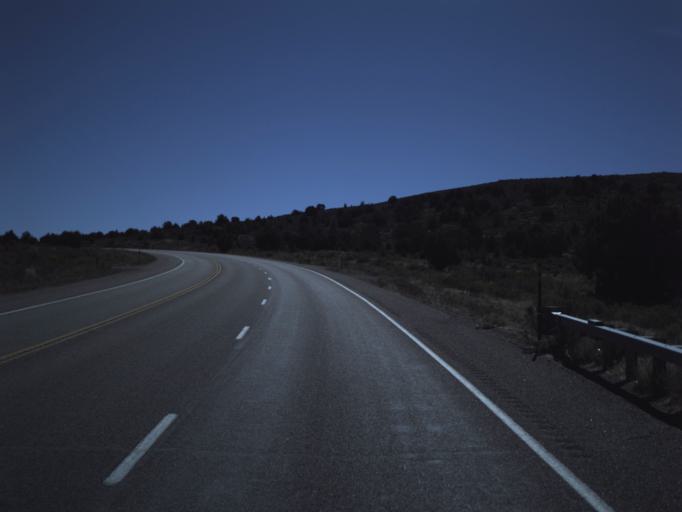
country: US
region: Utah
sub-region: Washington County
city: Ivins
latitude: 37.3238
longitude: -113.6926
